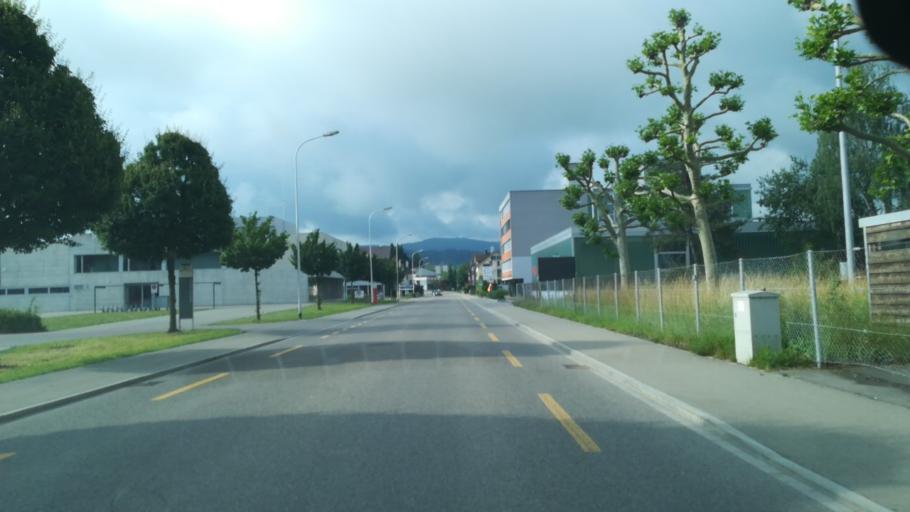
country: CH
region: Saint Gallen
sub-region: Wahlkreis St. Gallen
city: Gossau
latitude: 47.4229
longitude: 9.2414
